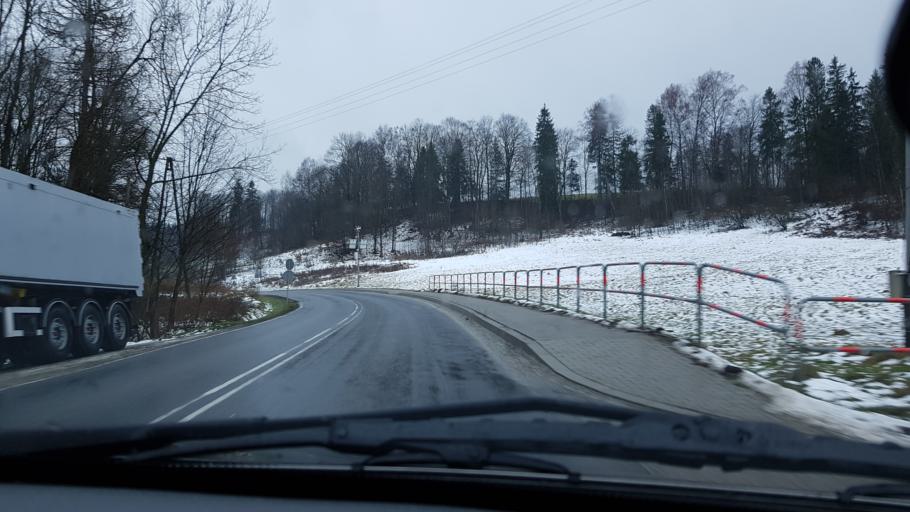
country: PL
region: Lesser Poland Voivodeship
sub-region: Powiat nowotarski
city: Raba Wyzna
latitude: 49.5369
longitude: 19.8884
